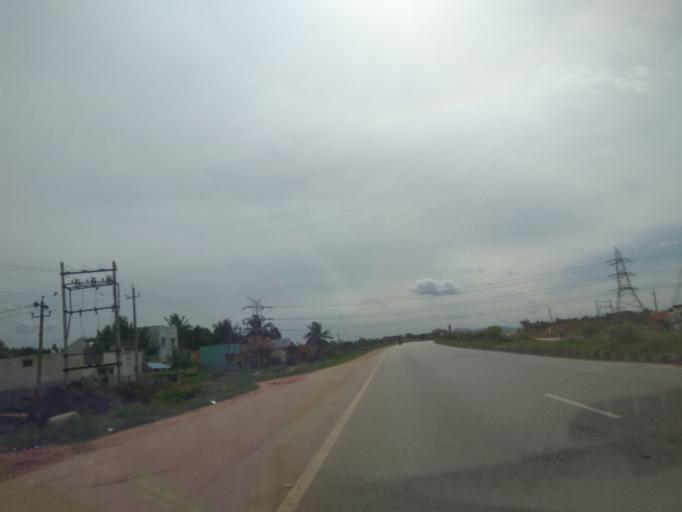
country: IN
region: Karnataka
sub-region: Bangalore Rural
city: Dasarahalli
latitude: 13.1338
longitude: 77.9467
